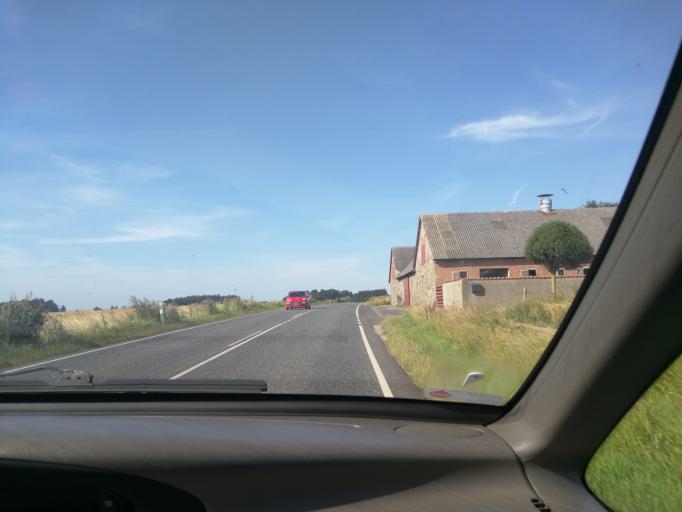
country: DK
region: Central Jutland
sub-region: Viborg Kommune
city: Bjerringbro
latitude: 56.3437
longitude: 9.6801
